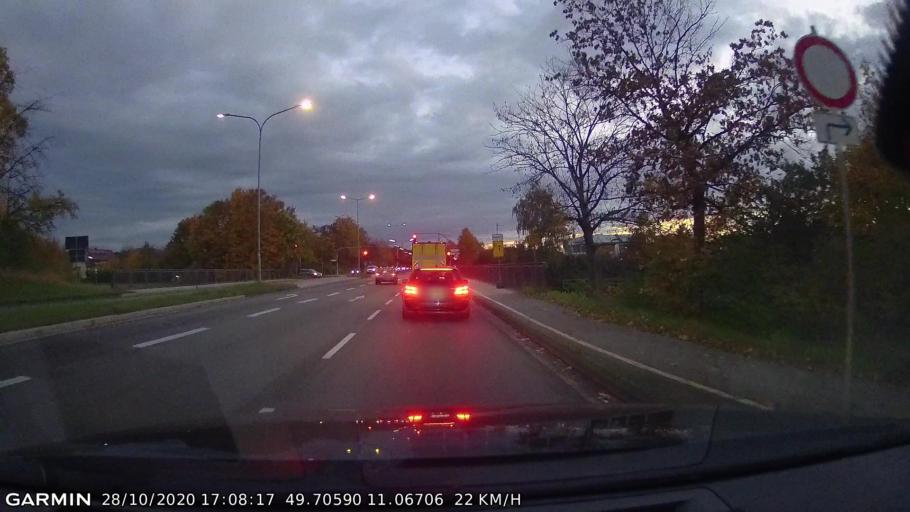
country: DE
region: Bavaria
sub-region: Upper Franconia
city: Forchheim
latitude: 49.7059
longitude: 11.0671
